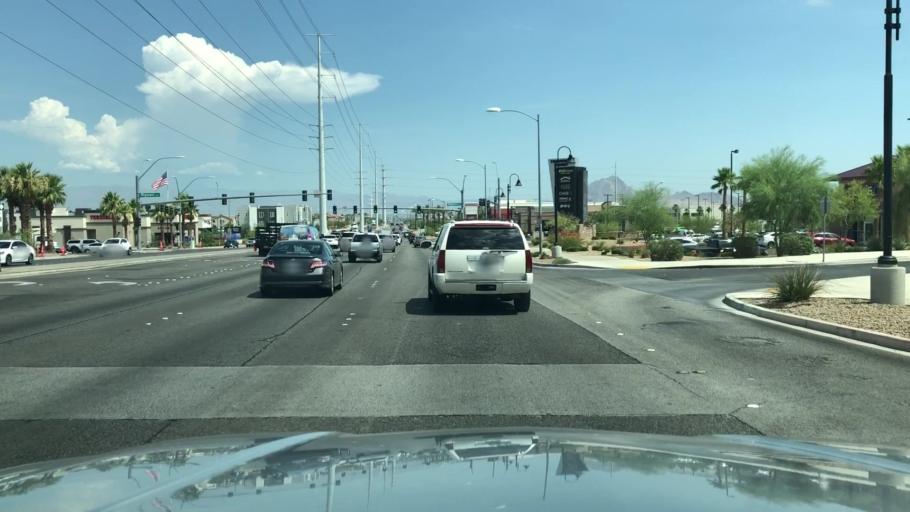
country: US
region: Nevada
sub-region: Clark County
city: Whitney
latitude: 36.0334
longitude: -115.0468
